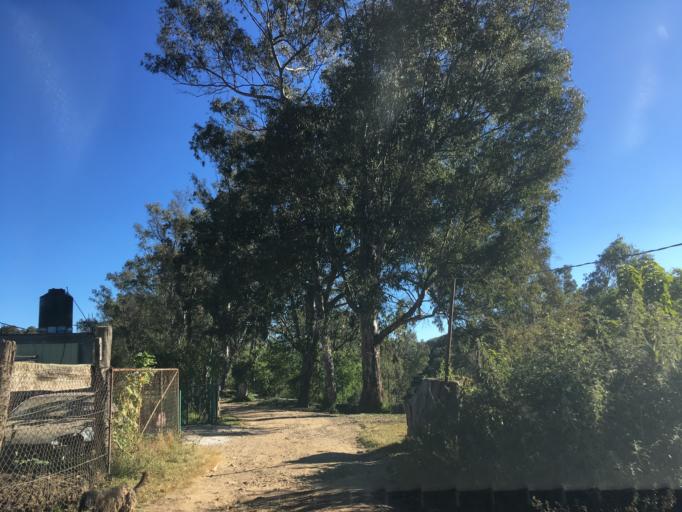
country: MX
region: Michoacan
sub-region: Morelia
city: Montana Monarca (Punta Altozano)
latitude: 19.6550
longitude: -101.1494
